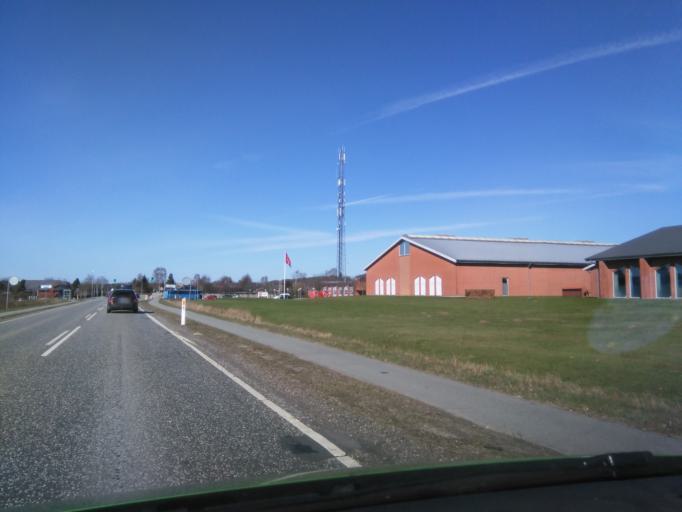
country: DK
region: Central Jutland
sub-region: Favrskov Kommune
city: Hinnerup
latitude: 56.2519
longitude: 10.0691
